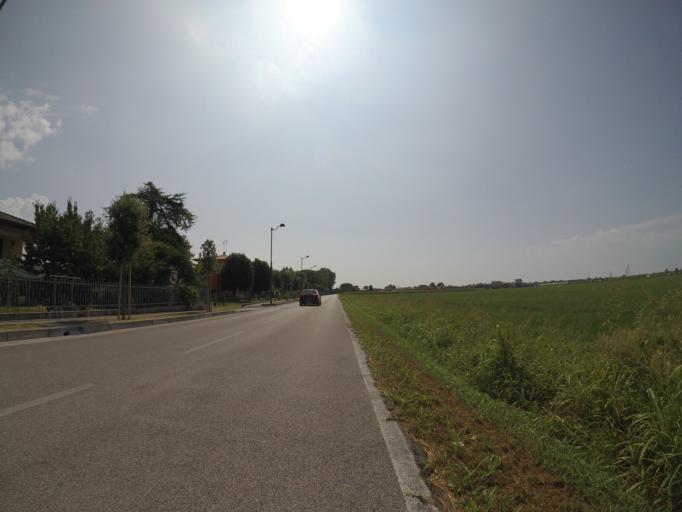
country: IT
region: Veneto
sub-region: Provincia di Venezia
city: Bibione
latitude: 45.6705
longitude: 13.0572
